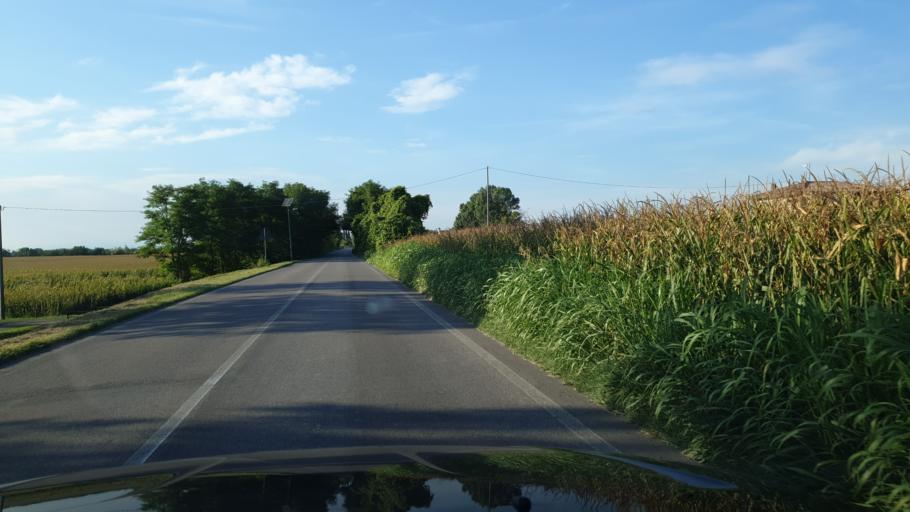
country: IT
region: Veneto
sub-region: Provincia di Rovigo
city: Fratta Polesine
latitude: 45.0135
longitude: 11.6409
